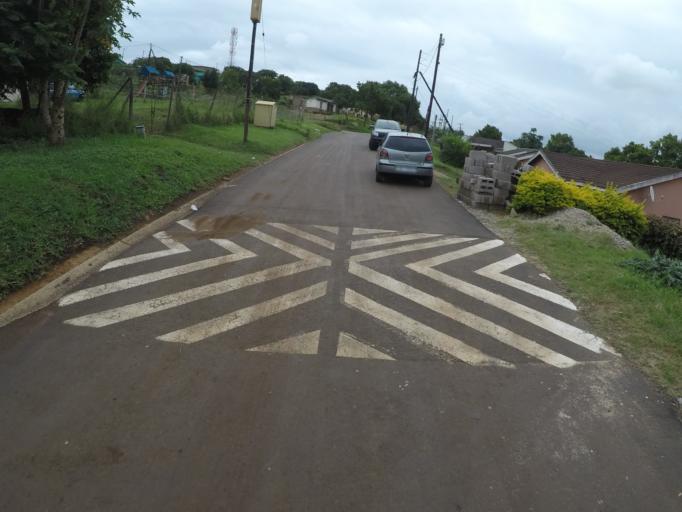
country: ZA
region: KwaZulu-Natal
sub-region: uThungulu District Municipality
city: Empangeni
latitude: -28.7678
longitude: 31.8606
